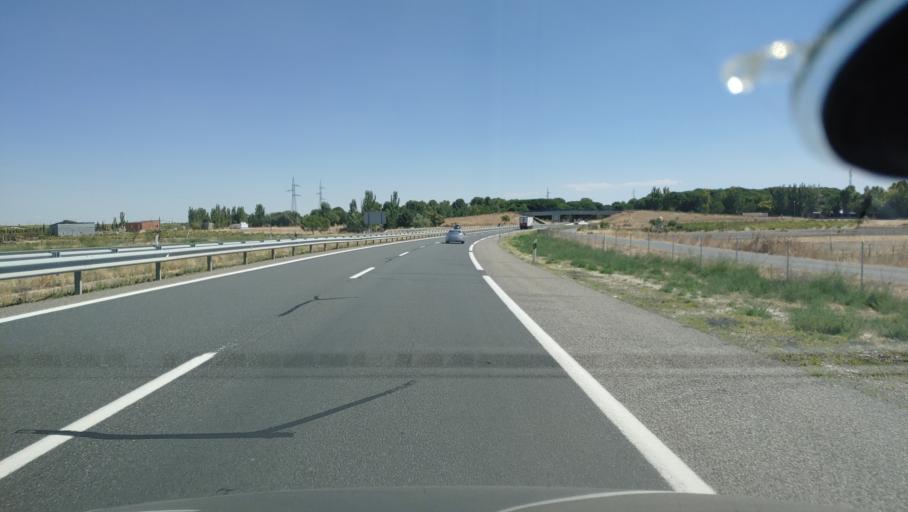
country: ES
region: Castille-La Mancha
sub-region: Provincia de Ciudad Real
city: Villarta de San Juan
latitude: 39.2450
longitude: -3.4192
